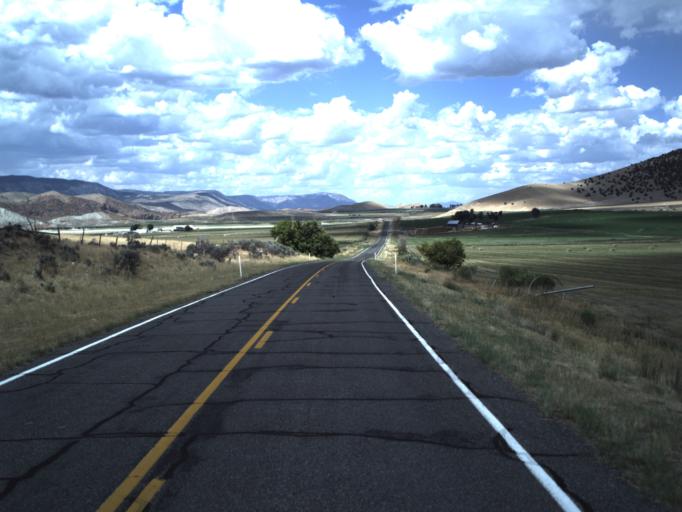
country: US
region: Utah
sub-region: Sanpete County
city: Gunnison
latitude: 39.1552
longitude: -111.7086
